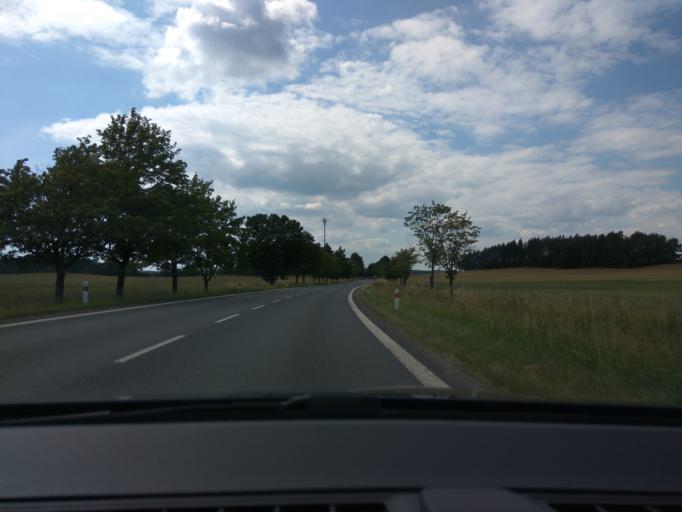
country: CZ
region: Jihocesky
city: Kovarov
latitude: 49.4694
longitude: 14.3039
